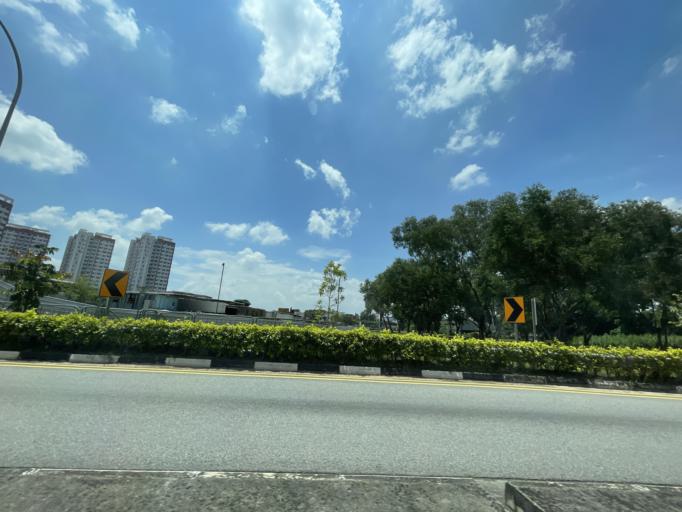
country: MY
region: Johor
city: Kampung Pasir Gudang Baru
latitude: 1.3814
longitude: 103.8794
